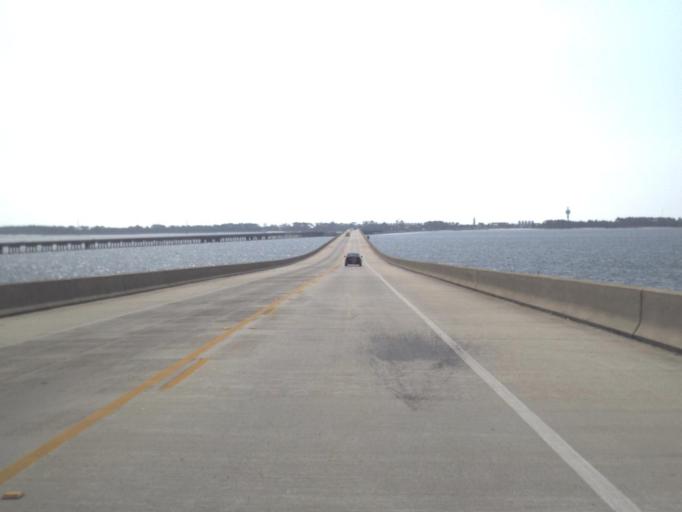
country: US
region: Florida
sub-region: Franklin County
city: Eastpoint
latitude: 29.6801
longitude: -84.8766
